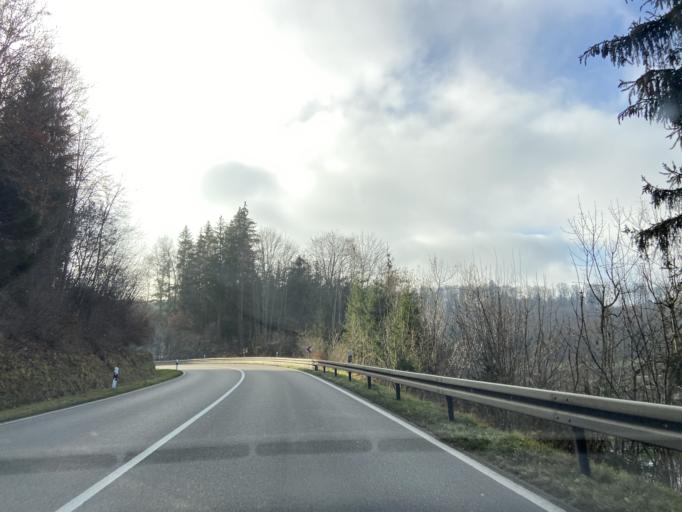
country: DE
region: Baden-Wuerttemberg
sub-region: Tuebingen Region
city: Hettingen
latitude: 48.2294
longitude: 9.2260
